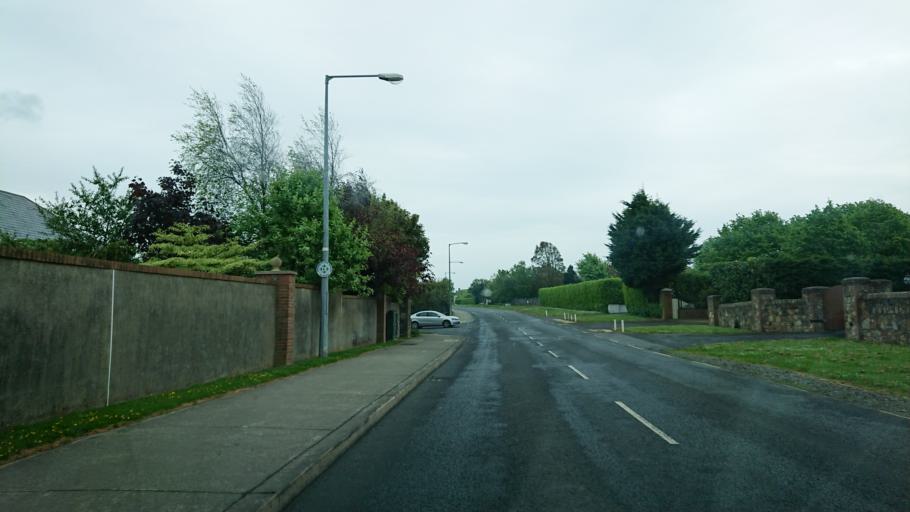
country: IE
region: Munster
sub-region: Waterford
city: Waterford
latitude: 52.2313
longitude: -7.0682
